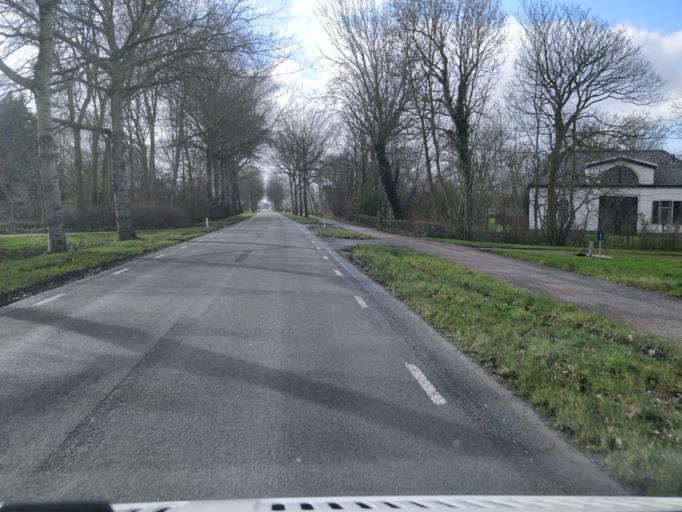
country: NL
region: Friesland
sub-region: Gemeente Franekeradeel
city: Sexbierum
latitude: 53.2172
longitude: 5.4766
